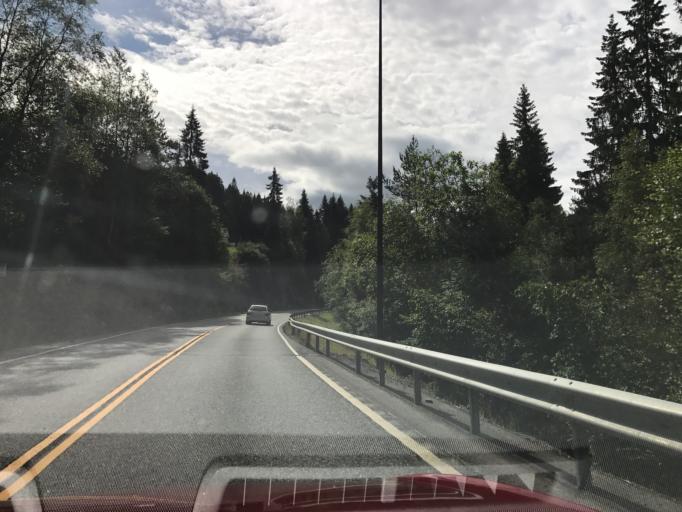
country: NO
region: Hordaland
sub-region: Voss
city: Voss
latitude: 60.6207
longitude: 6.5331
